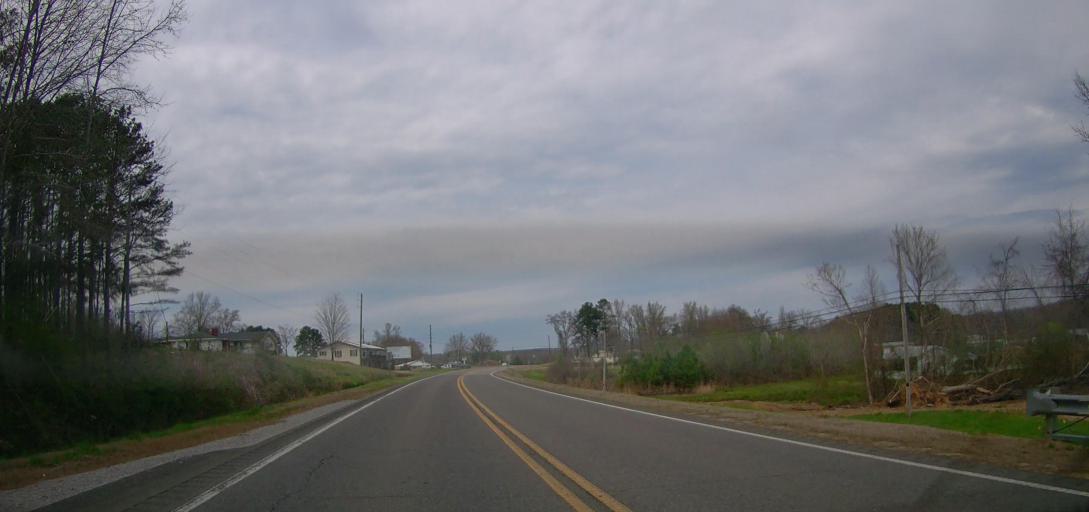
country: US
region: Alabama
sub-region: Marion County
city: Hamilton
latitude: 34.0972
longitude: -87.9879
